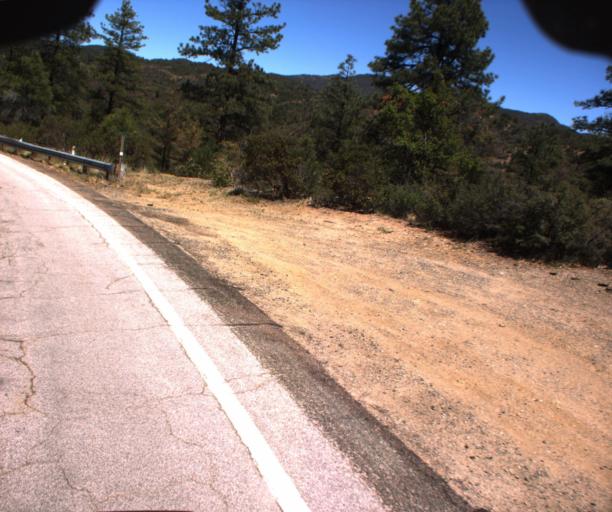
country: US
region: Arizona
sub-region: Yavapai County
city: Prescott
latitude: 34.4382
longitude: -112.5462
